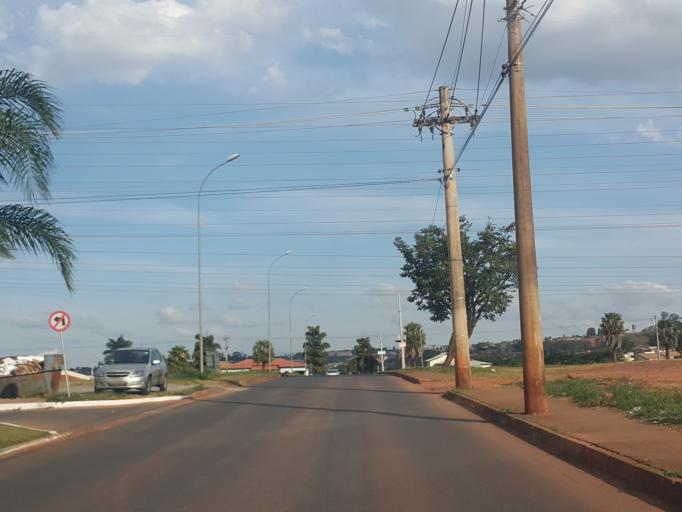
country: BR
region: Federal District
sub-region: Brasilia
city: Brasilia
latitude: -15.8434
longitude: -48.0222
